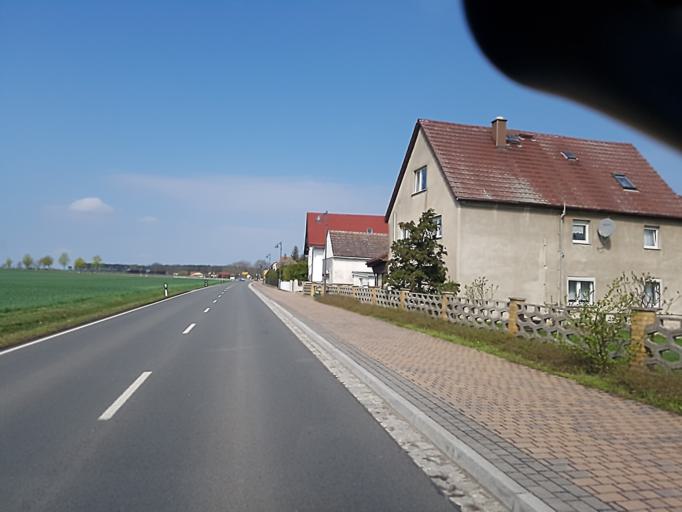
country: DE
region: Saxony
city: Zinna
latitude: 51.5657
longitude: 12.9166
